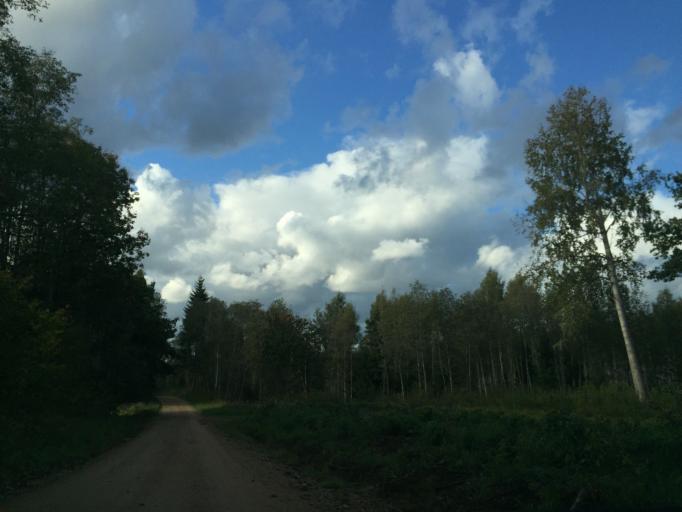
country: LV
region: Ligatne
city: Ligatne
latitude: 57.1324
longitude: 25.1016
